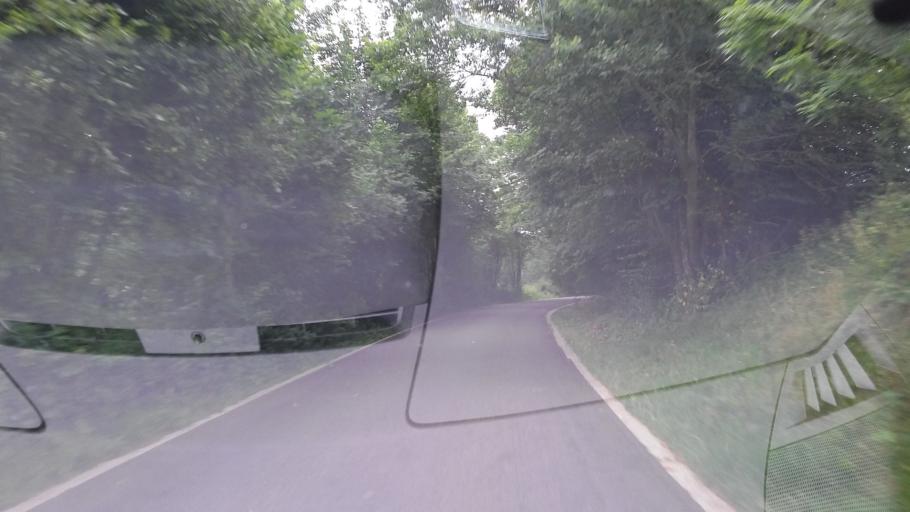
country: BE
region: Wallonia
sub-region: Province du Luxembourg
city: Arlon
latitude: 49.6684
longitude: 5.8346
